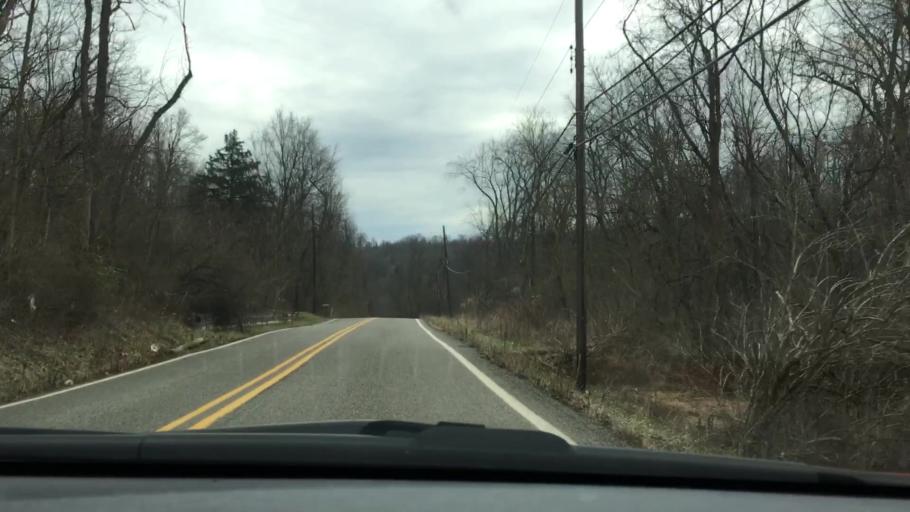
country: US
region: Pennsylvania
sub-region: Allegheny County
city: Sturgeon
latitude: 40.3941
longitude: -80.2029
